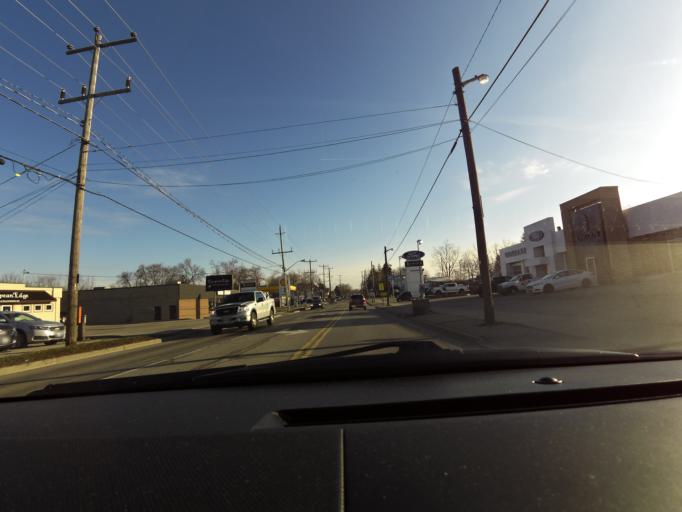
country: CA
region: Ontario
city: Ancaster
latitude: 43.0679
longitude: -79.9560
